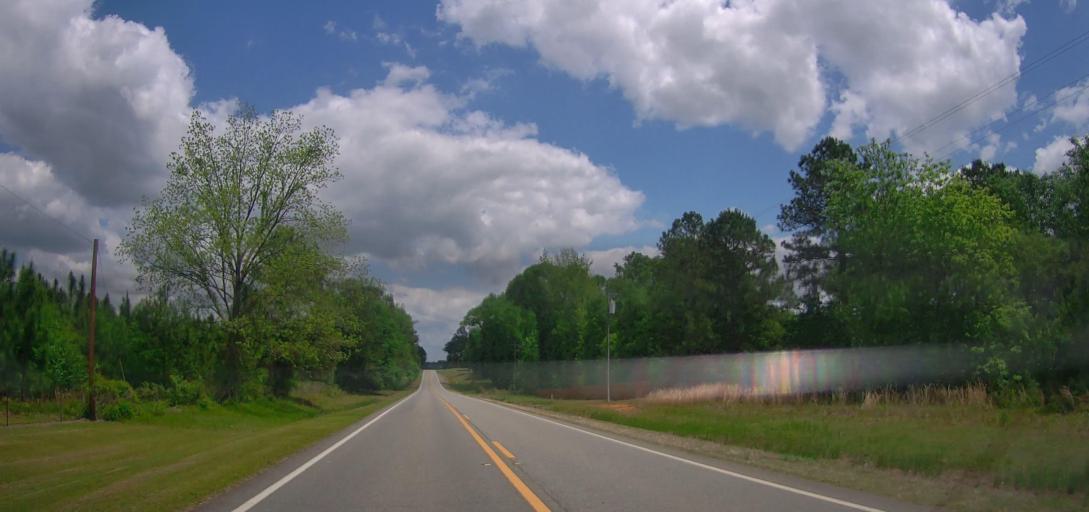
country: US
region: Georgia
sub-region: Laurens County
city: Dublin
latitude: 32.5462
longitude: -83.0666
